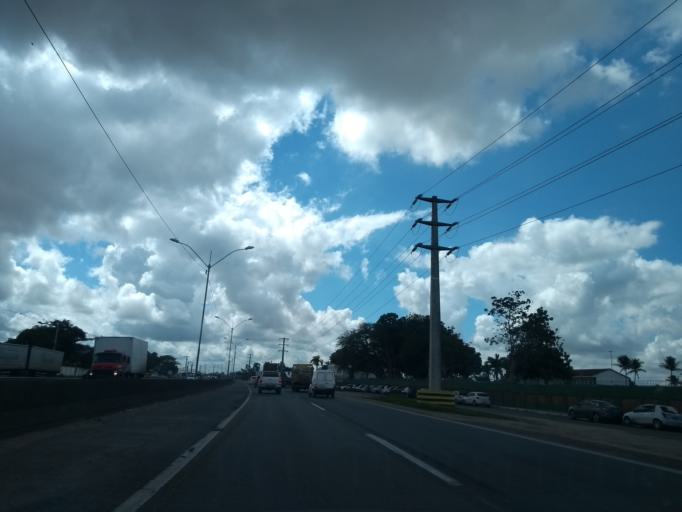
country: BR
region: Bahia
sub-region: Feira De Santana
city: Feira de Santana
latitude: -12.2796
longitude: -38.9419
